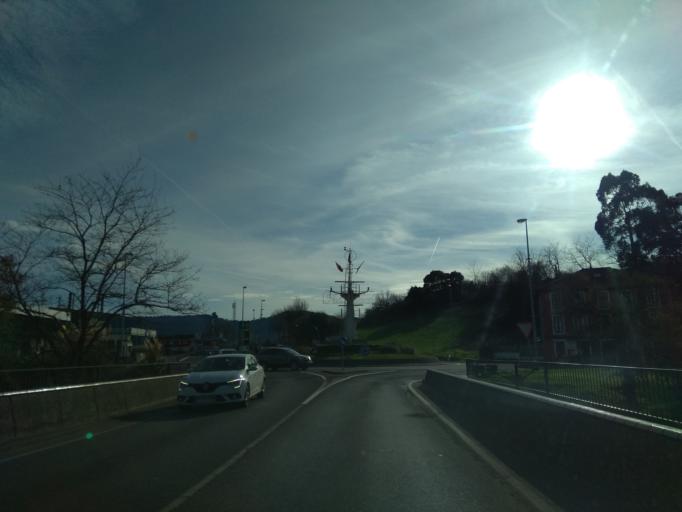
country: ES
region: Cantabria
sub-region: Provincia de Cantabria
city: El Astillero
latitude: 43.4124
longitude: -3.8436
